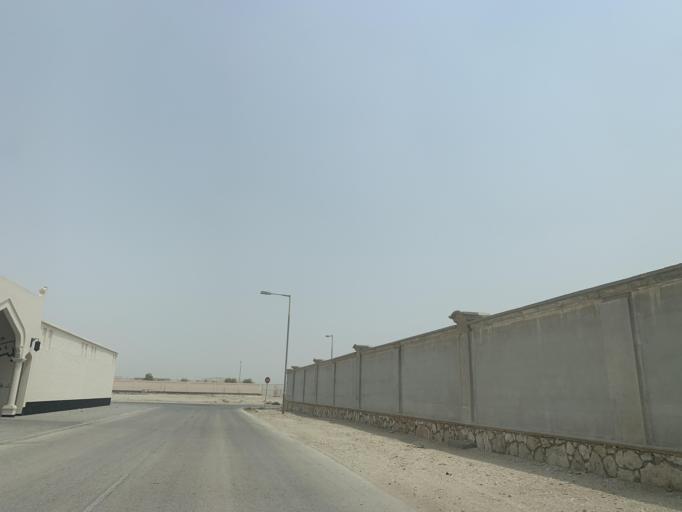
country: BH
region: Central Governorate
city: Madinat Hamad
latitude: 26.1620
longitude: 50.4816
